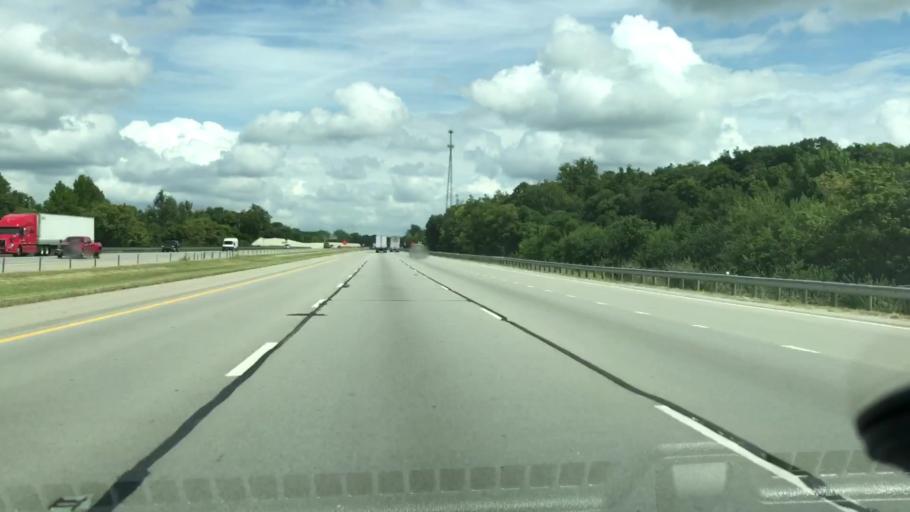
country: US
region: Ohio
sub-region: Clark County
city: Enon
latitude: 39.8893
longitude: -83.9293
